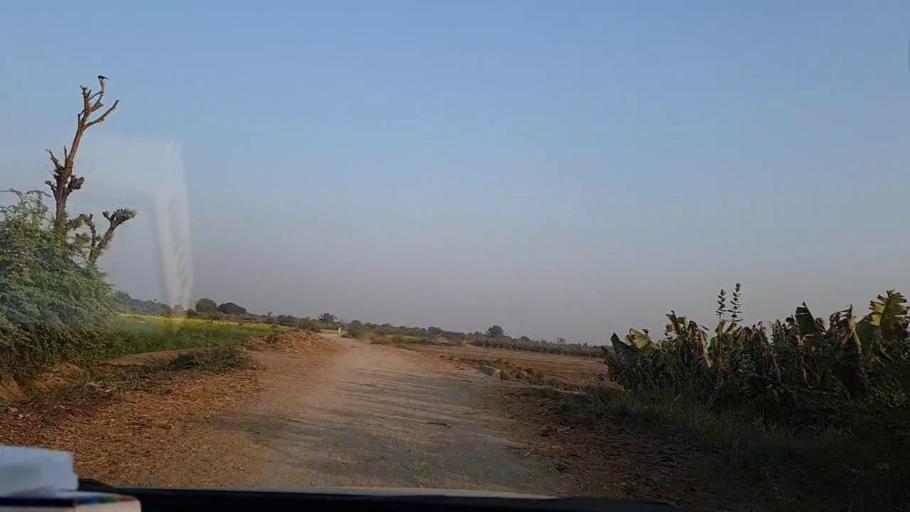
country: PK
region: Sindh
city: Tando Ghulam Ali
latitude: 25.1864
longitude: 68.9117
